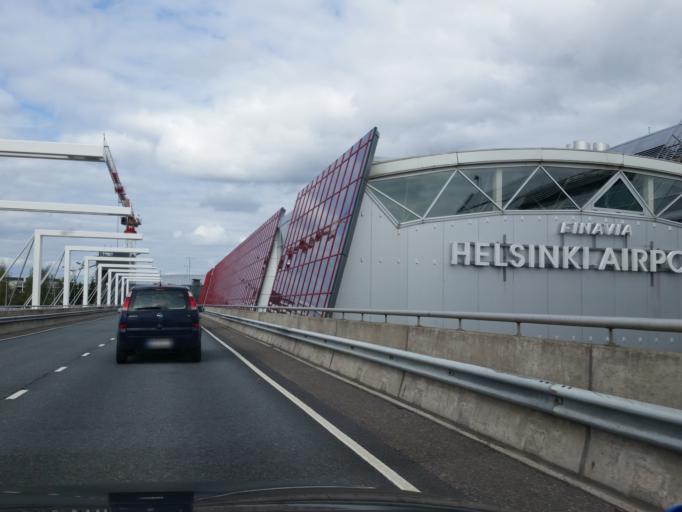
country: FI
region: Uusimaa
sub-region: Helsinki
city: Vantaa
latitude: 60.3152
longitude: 24.9718
